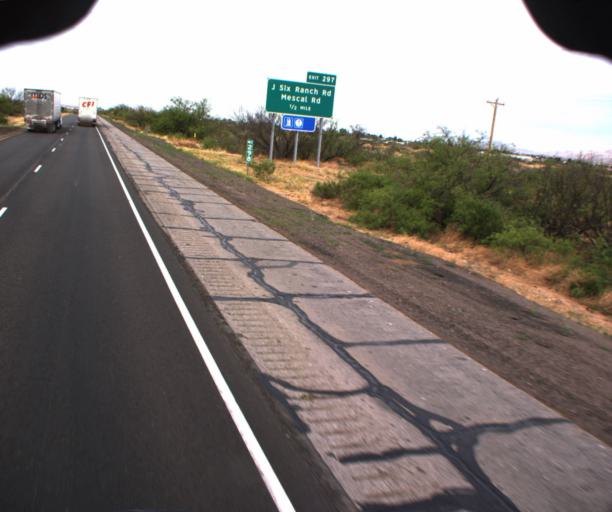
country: US
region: Arizona
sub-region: Cochise County
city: Mescal
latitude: 31.9632
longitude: -110.4202
